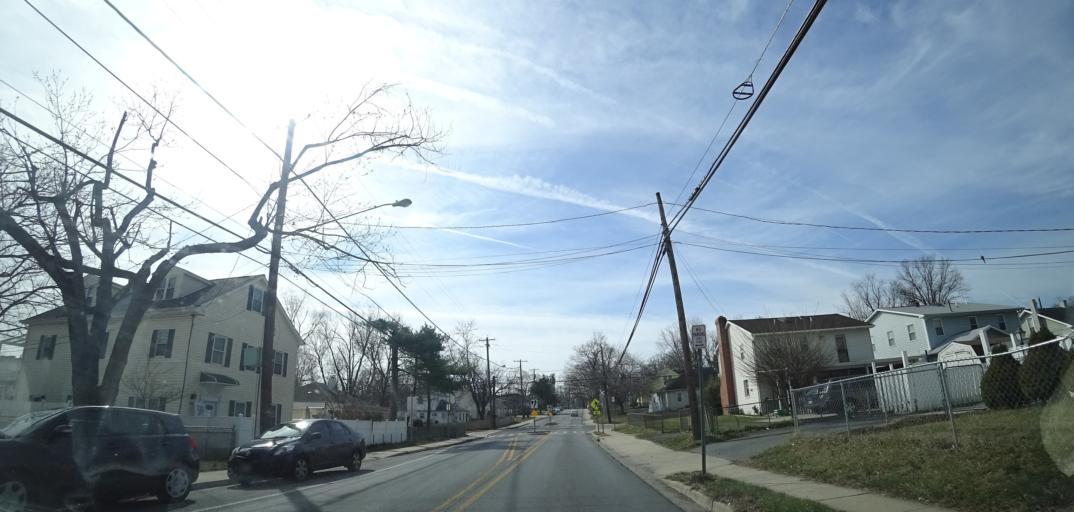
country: US
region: Maryland
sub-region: Montgomery County
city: Rockville
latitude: 39.0894
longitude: -77.1434
